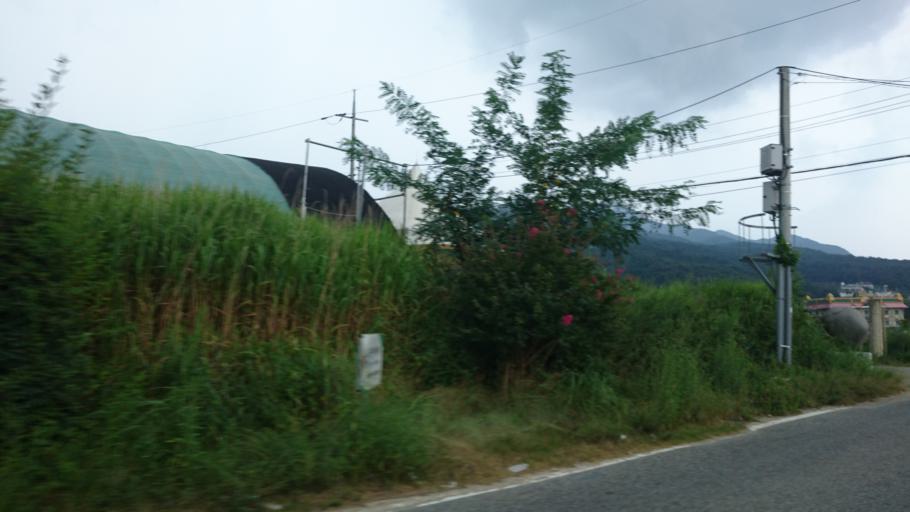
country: KR
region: Daegu
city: Daegu
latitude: 36.0022
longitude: 128.5997
